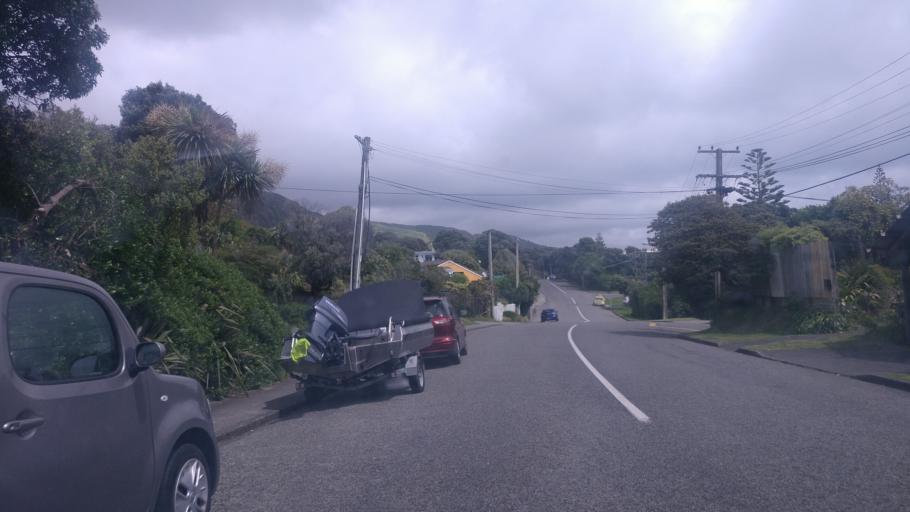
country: NZ
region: Wellington
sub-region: Kapiti Coast District
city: Paraparaumu
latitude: -40.9781
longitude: 174.9593
